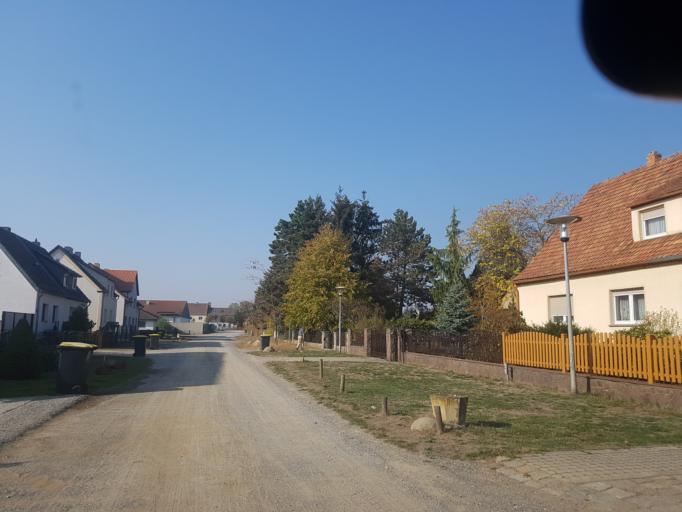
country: DE
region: Brandenburg
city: Finsterwalde
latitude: 51.6188
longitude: 13.7171
